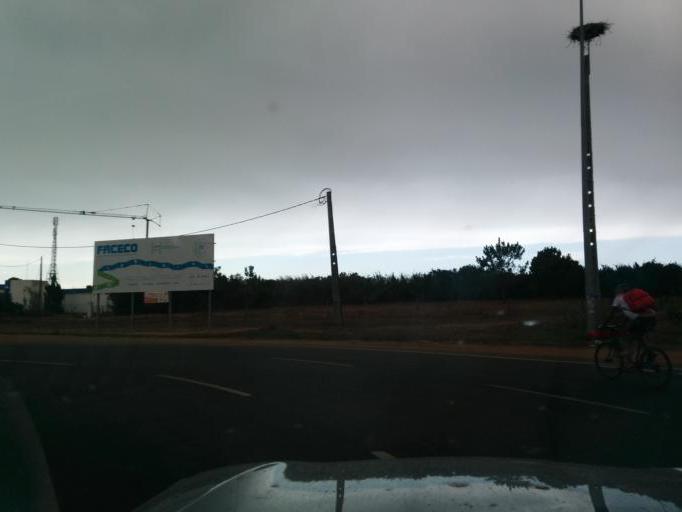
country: PT
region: Beja
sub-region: Odemira
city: Vila Nova de Milfontes
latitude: 37.7335
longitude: -8.7715
